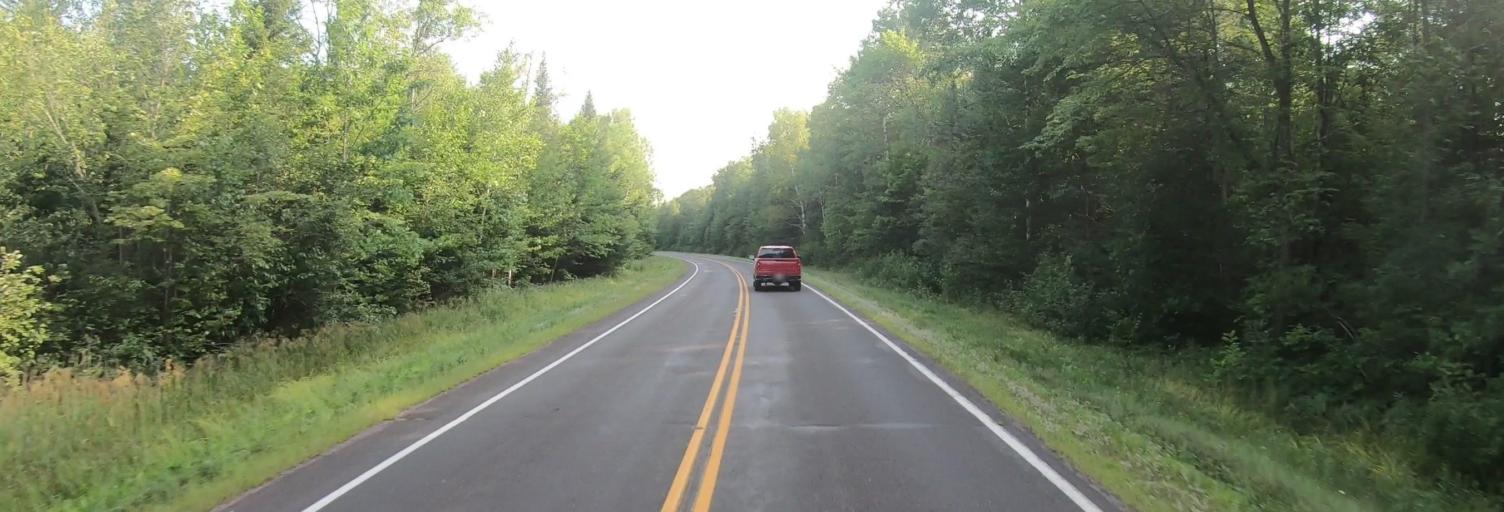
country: US
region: Wisconsin
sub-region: Ashland County
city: Ashland
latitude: 46.2279
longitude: -90.8380
